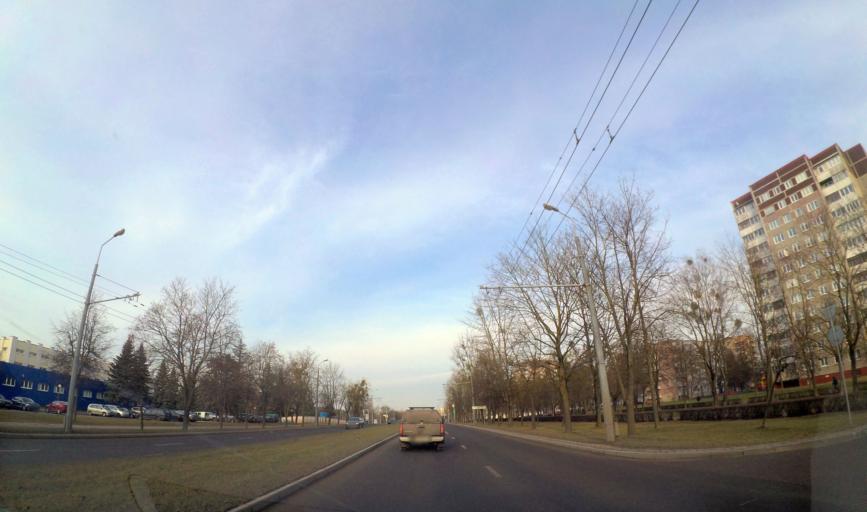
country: BY
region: Grodnenskaya
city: Hrodna
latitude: 53.6911
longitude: 23.8009
